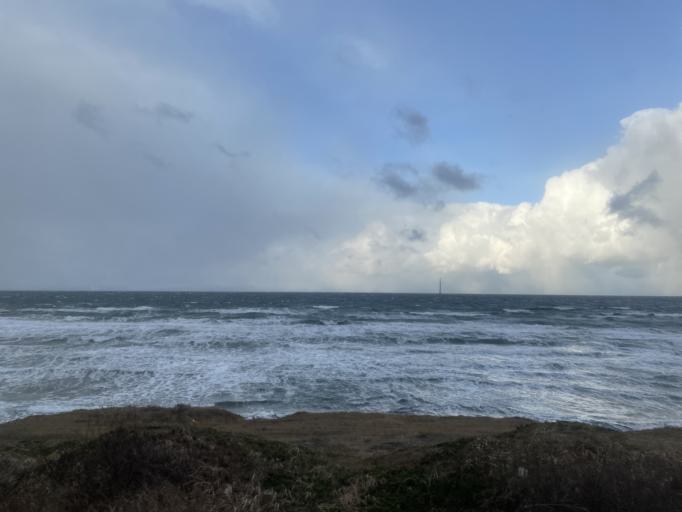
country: JP
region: Aomori
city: Mutsu
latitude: 40.9731
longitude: 141.2221
